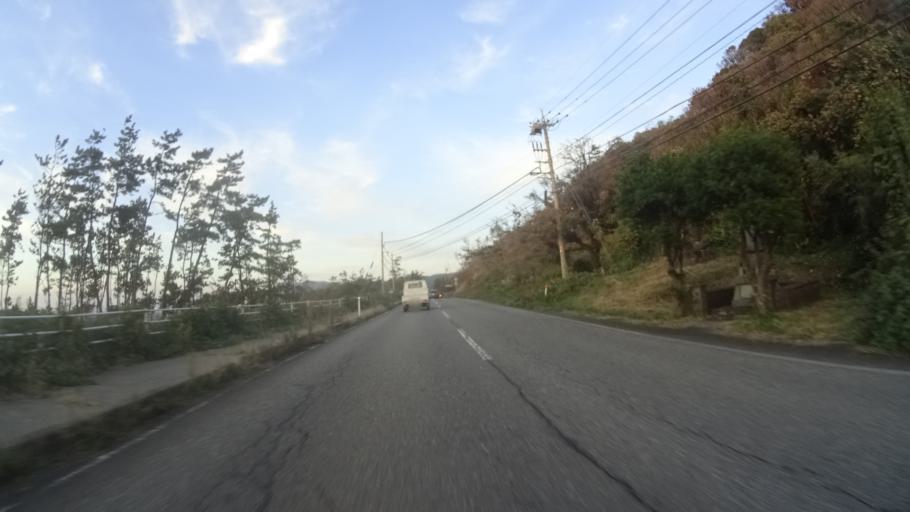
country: JP
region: Ishikawa
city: Nanao
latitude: 37.2660
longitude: 136.7280
